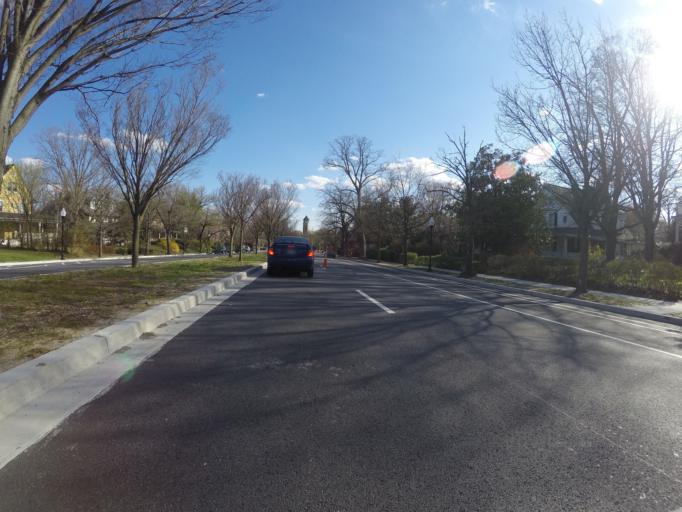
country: US
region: Maryland
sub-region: City of Baltimore
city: Baltimore
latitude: 39.3462
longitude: -76.6358
